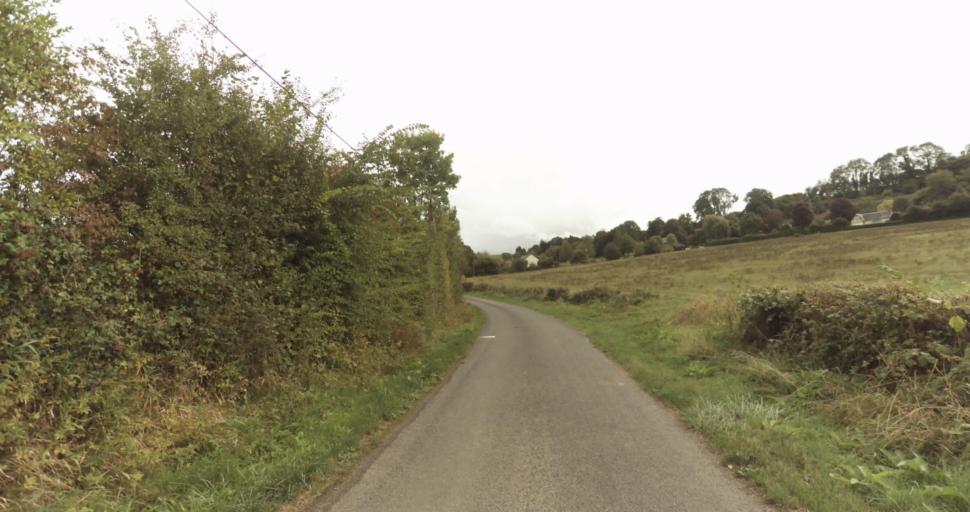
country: FR
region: Lower Normandy
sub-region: Departement de l'Orne
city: Gace
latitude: 48.8132
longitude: 0.2969
